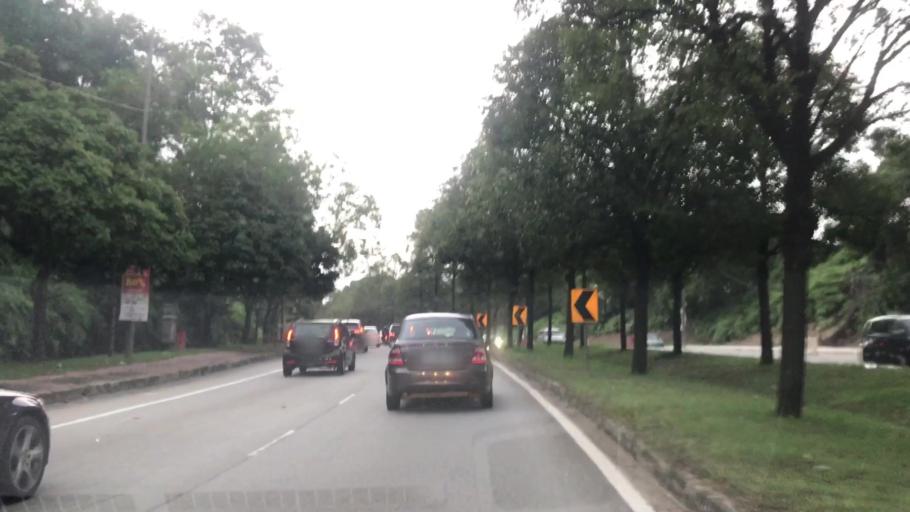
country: MY
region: Selangor
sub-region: Petaling
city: Petaling Jaya
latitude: 3.0557
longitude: 101.6658
